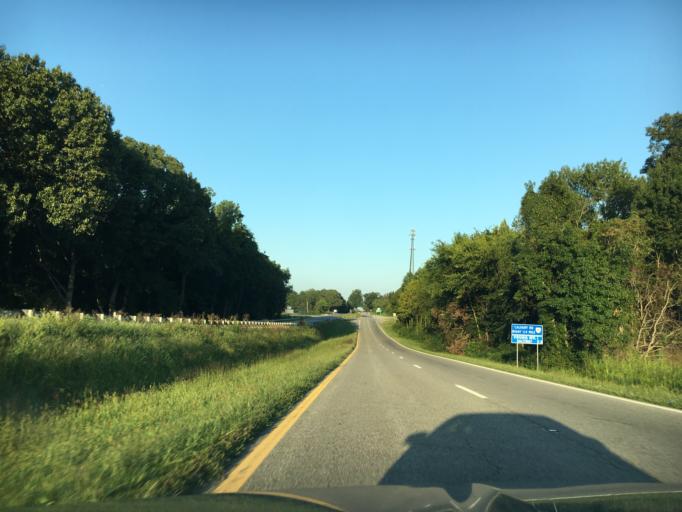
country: US
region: Virginia
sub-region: Halifax County
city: Mountain Road
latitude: 36.5841
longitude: -79.1432
